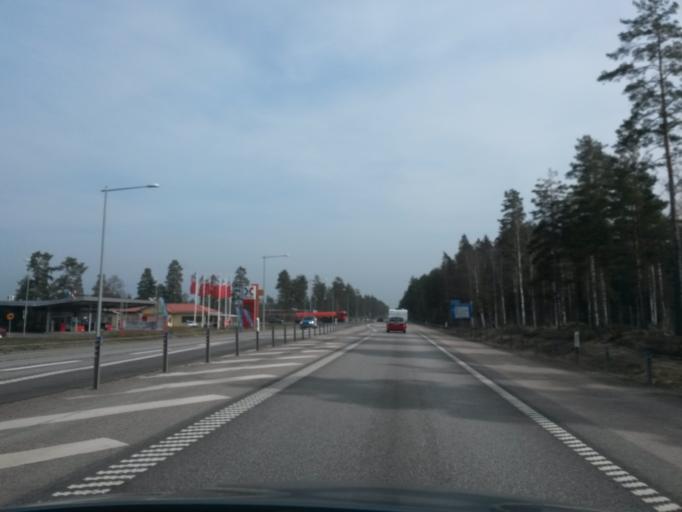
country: SE
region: OErebro
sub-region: Laxa Kommun
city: Laxa
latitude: 58.9849
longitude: 14.6353
